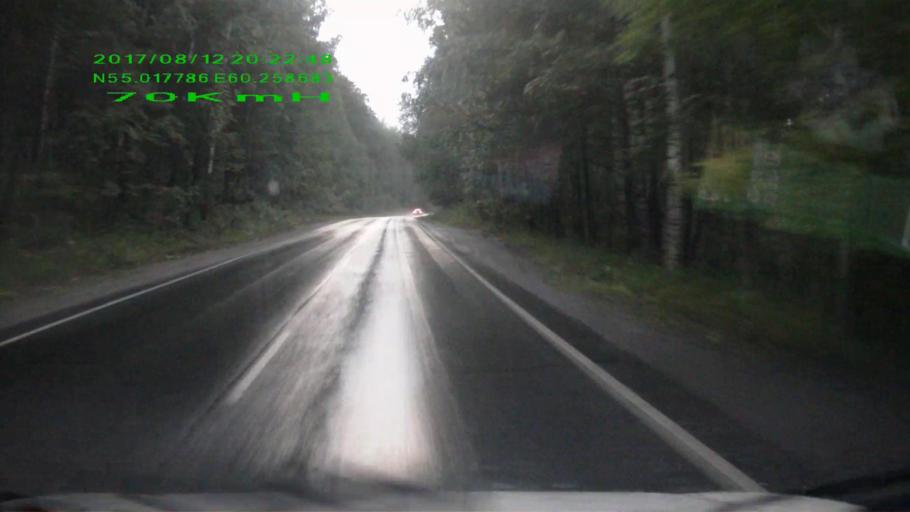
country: RU
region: Chelyabinsk
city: Chebarkul'
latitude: 55.0180
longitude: 60.2583
